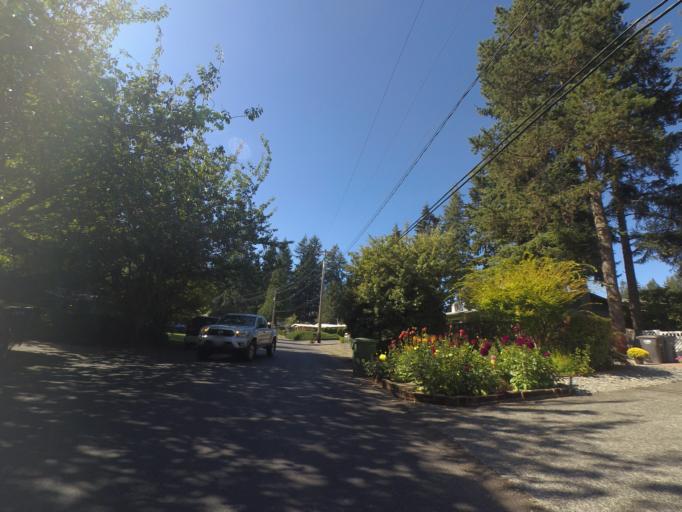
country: US
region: Washington
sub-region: Pierce County
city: Fircrest
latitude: 47.2139
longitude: -122.5233
